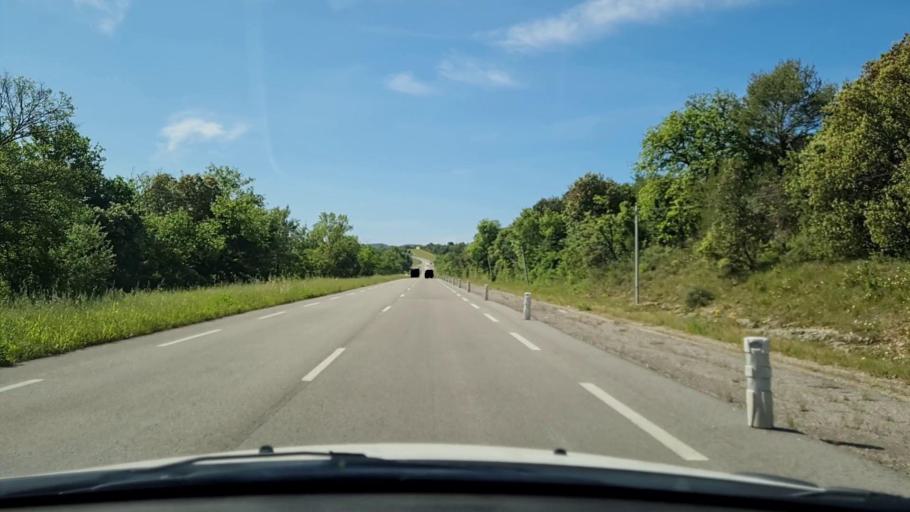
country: FR
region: Languedoc-Roussillon
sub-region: Departement du Gard
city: Vezenobres
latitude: 44.0362
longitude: 4.1486
